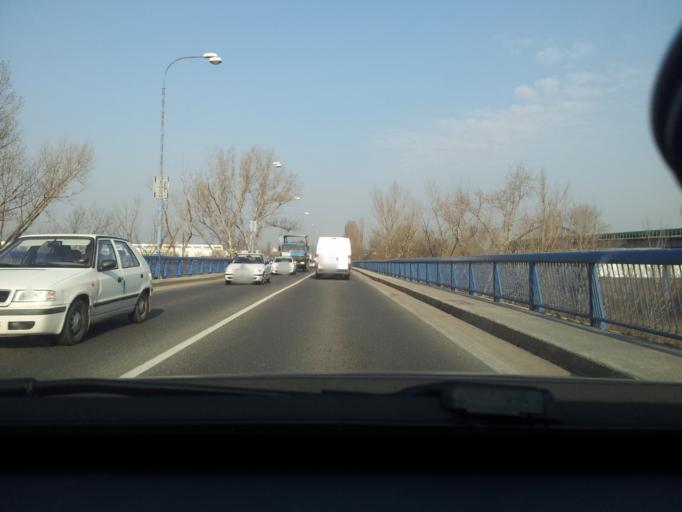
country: SK
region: Trnavsky
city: Hlohovec
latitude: 48.4301
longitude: 17.7919
